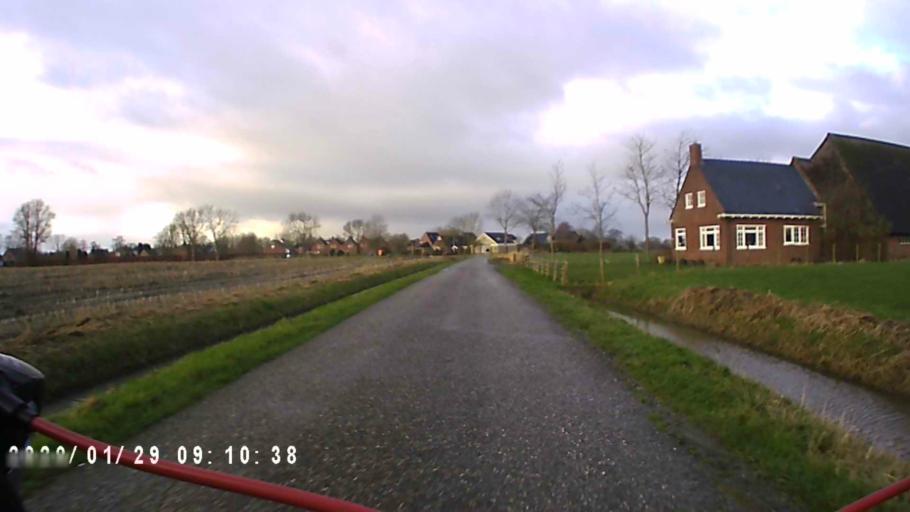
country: NL
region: Groningen
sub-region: Gemeente Zuidhorn
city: Oldehove
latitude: 53.3113
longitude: 6.4500
